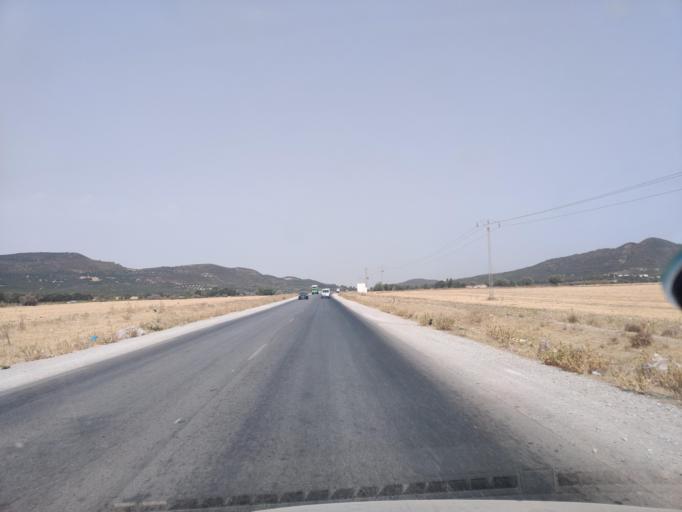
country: TN
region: Tunis
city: Hammam-Lif
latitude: 36.6230
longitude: 10.4047
